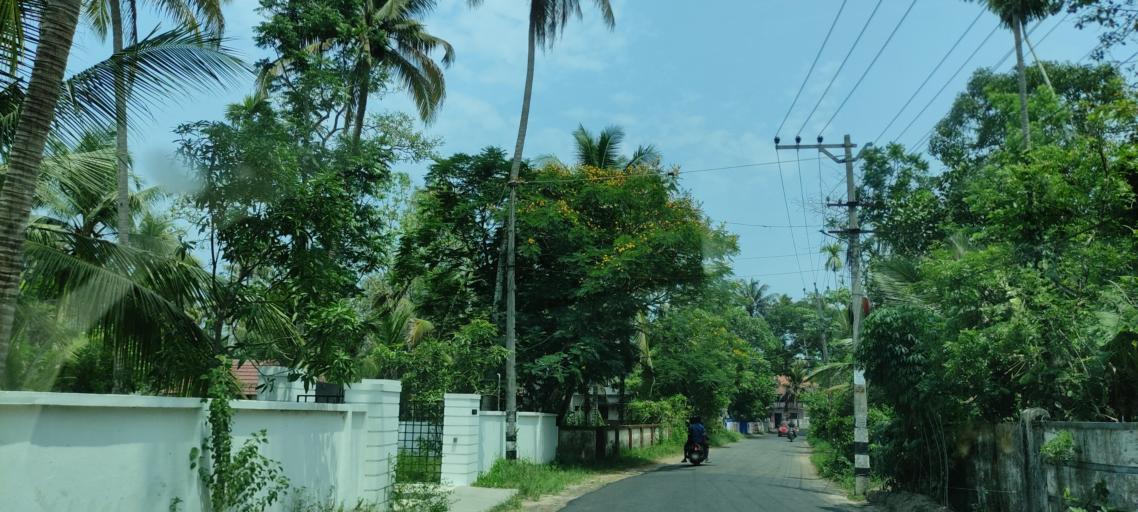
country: IN
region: Kerala
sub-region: Alappuzha
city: Vayalar
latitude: 9.7074
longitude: 76.3379
